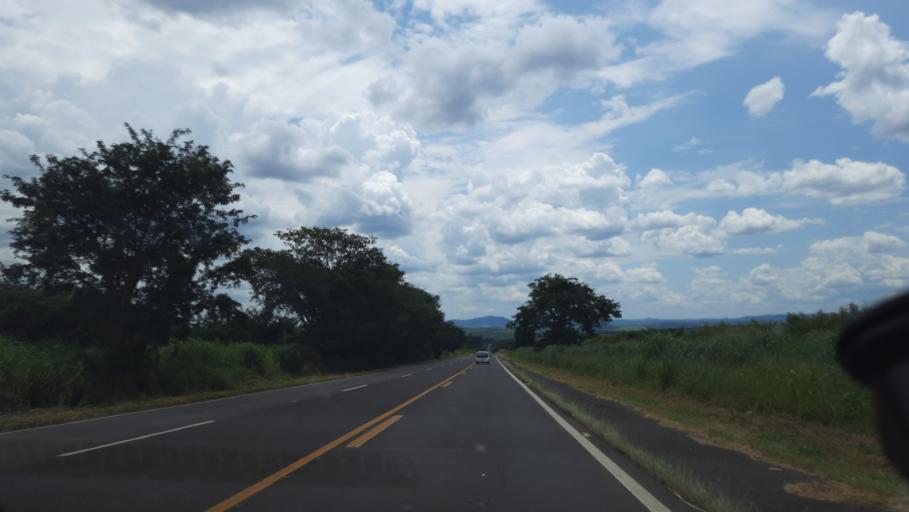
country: BR
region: Sao Paulo
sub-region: Mococa
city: Mococa
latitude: -21.4845
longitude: -47.0820
